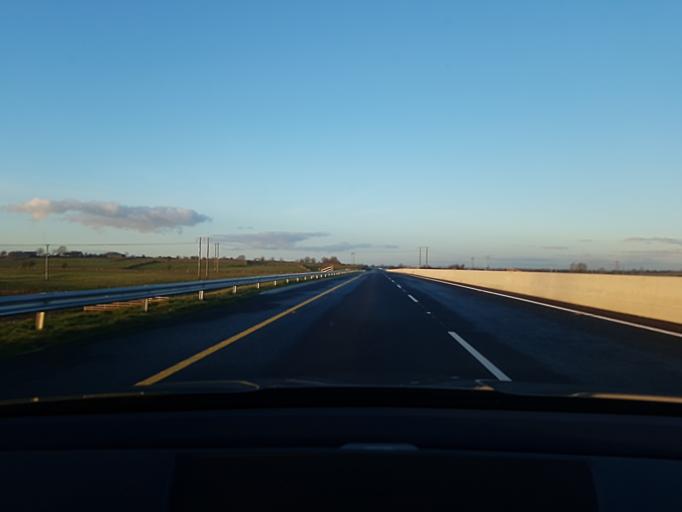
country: IE
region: Connaught
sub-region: County Galway
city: Tuam
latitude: 53.4751
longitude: -8.8639
